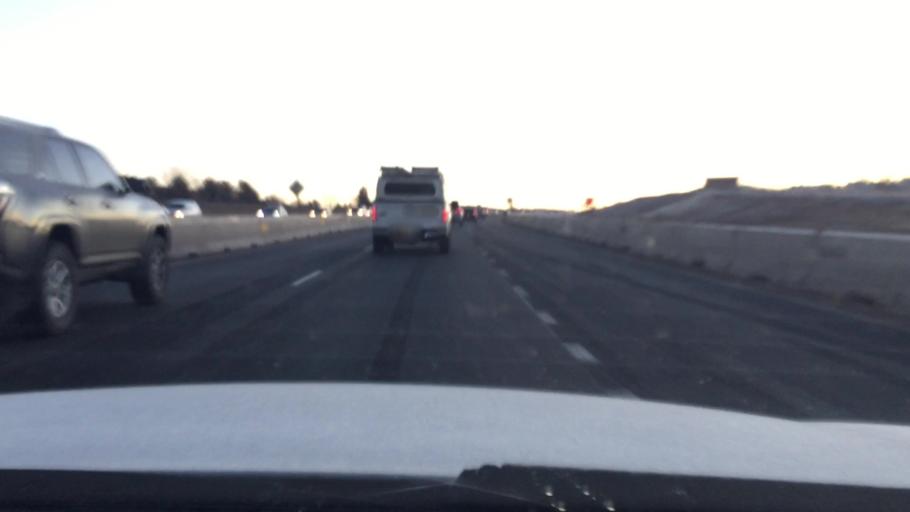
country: US
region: Colorado
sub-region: Douglas County
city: Highlands Ranch
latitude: 39.5653
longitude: -104.9819
